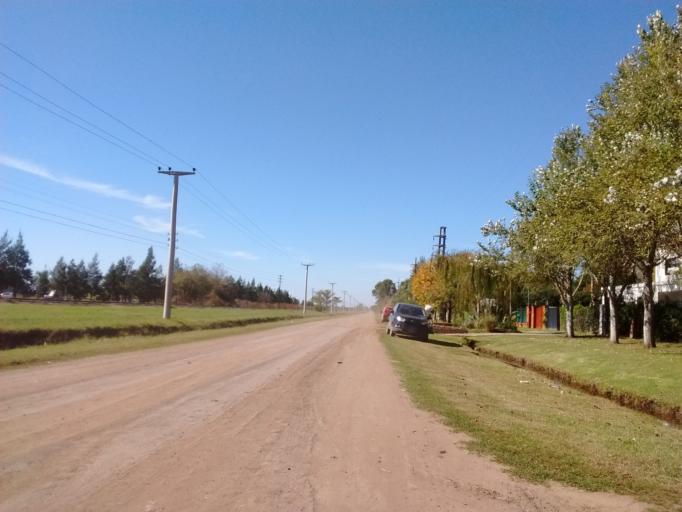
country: AR
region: Santa Fe
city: Roldan
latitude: -32.9079
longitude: -60.8630
